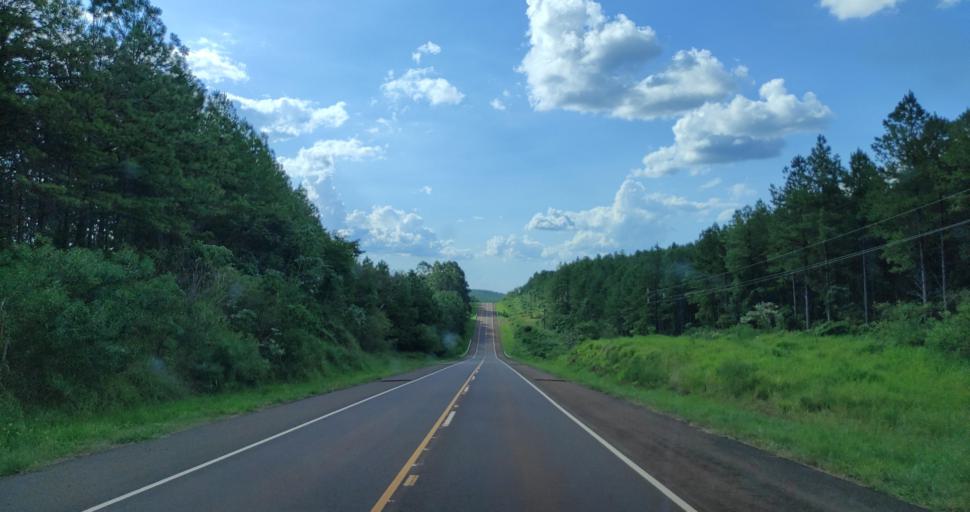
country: AR
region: Misiones
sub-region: Departamento de San Pedro
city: San Pedro
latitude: -26.3656
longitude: -53.9474
